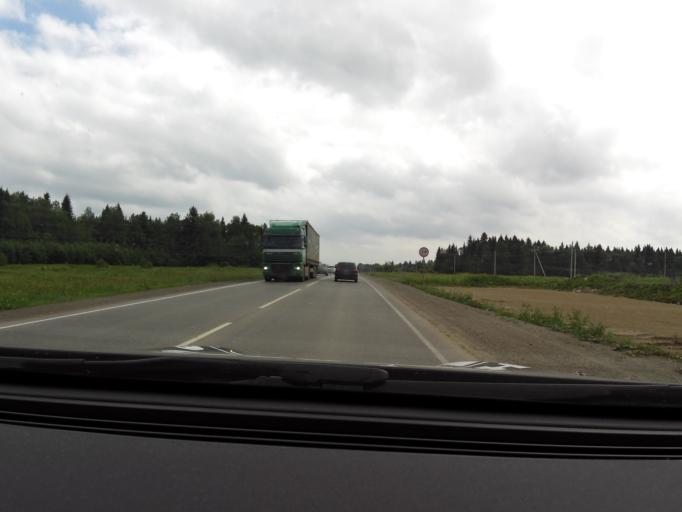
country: RU
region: Perm
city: Kukushtan
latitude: 57.6300
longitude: 56.4642
